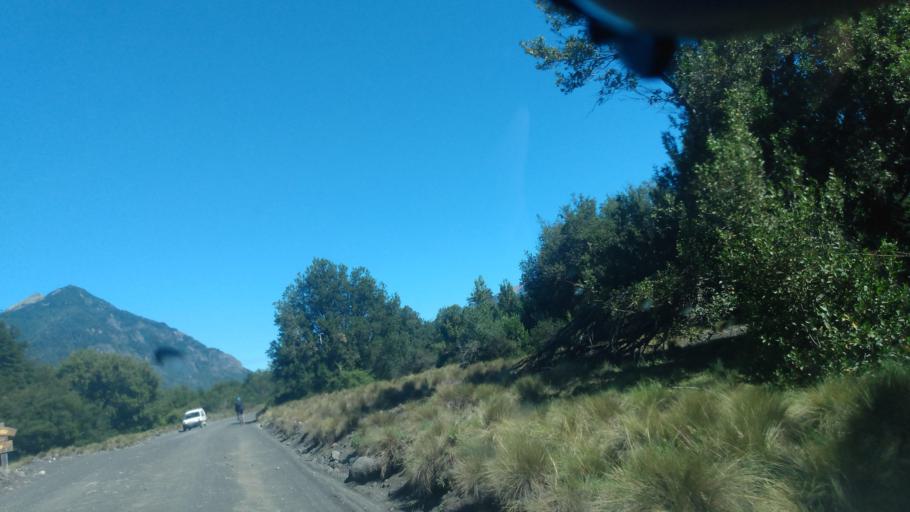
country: AR
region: Neuquen
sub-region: Departamento de Lacar
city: San Martin de los Andes
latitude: -39.7470
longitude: -71.5037
